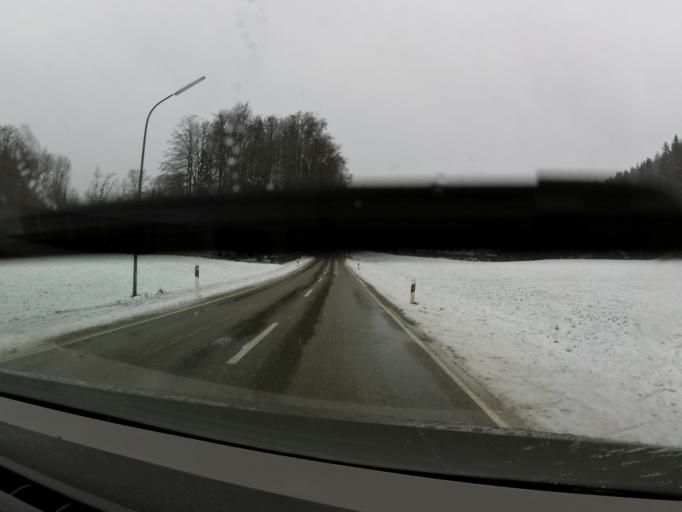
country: DE
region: Bavaria
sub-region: Upper Bavaria
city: Gmund am Tegernsee
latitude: 47.7506
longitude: 11.7218
